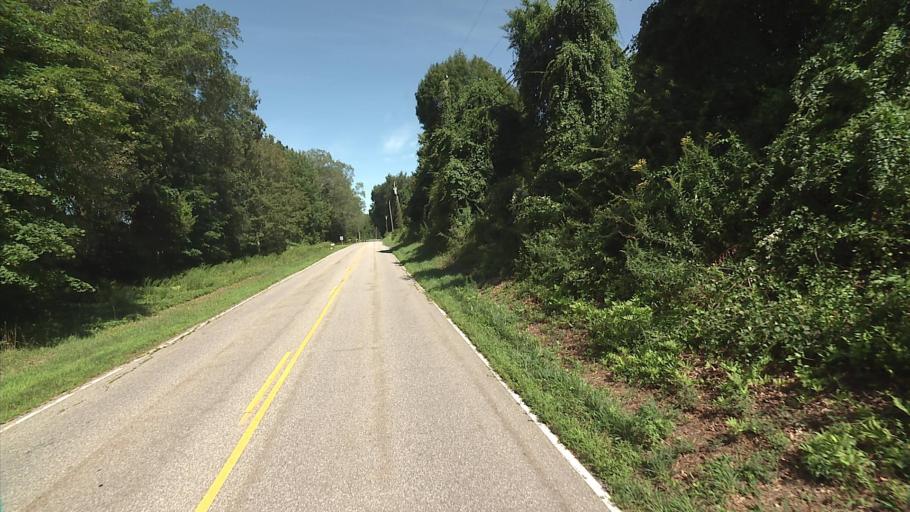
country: US
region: Connecticut
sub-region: New London County
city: Baltic
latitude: 41.6463
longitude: -72.0907
